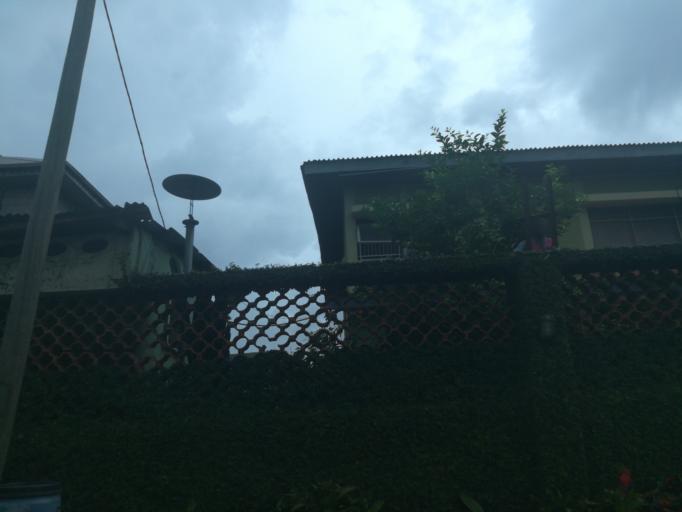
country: NG
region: Lagos
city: Ikeja
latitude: 6.6151
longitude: 3.3473
